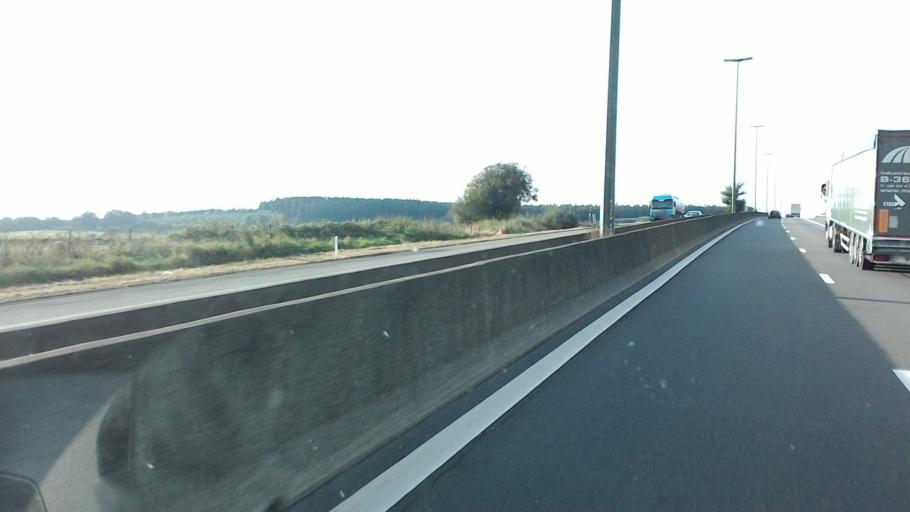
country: BE
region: Wallonia
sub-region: Province du Luxembourg
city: Leglise
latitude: 49.7781
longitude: 5.5420
